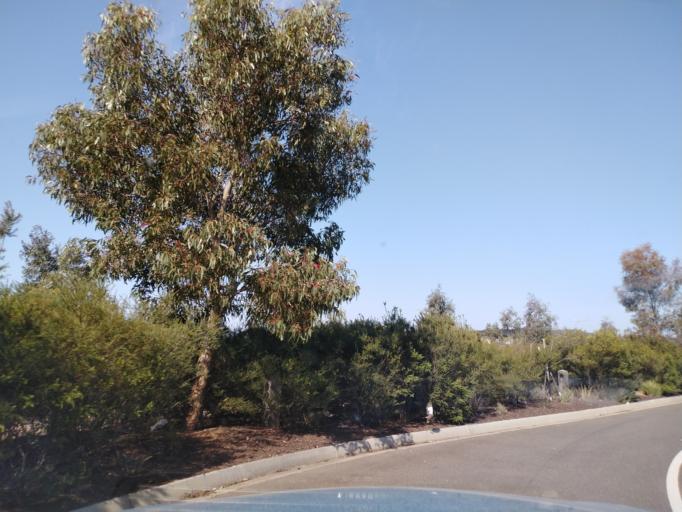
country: AU
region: Victoria
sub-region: Wyndham
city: Williams Landing
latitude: -37.8419
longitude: 144.7392
